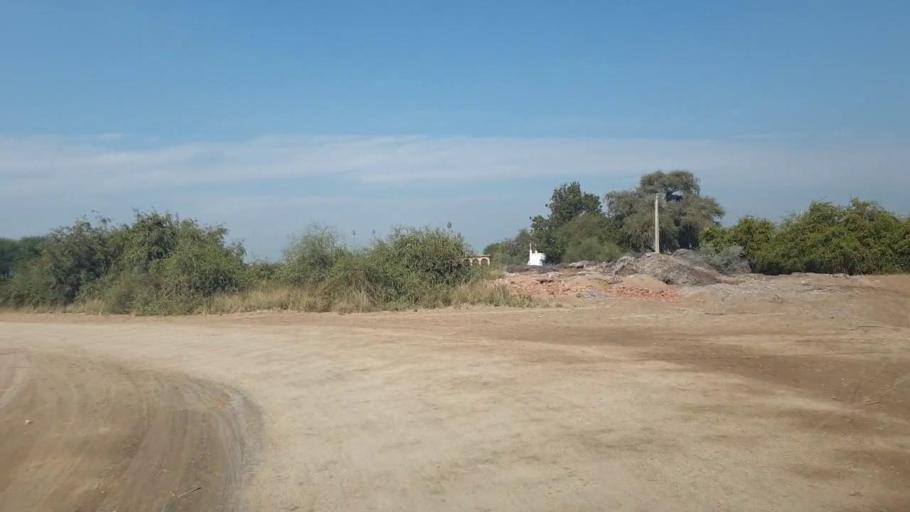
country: PK
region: Sindh
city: Shahdadpur
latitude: 25.9812
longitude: 68.5292
